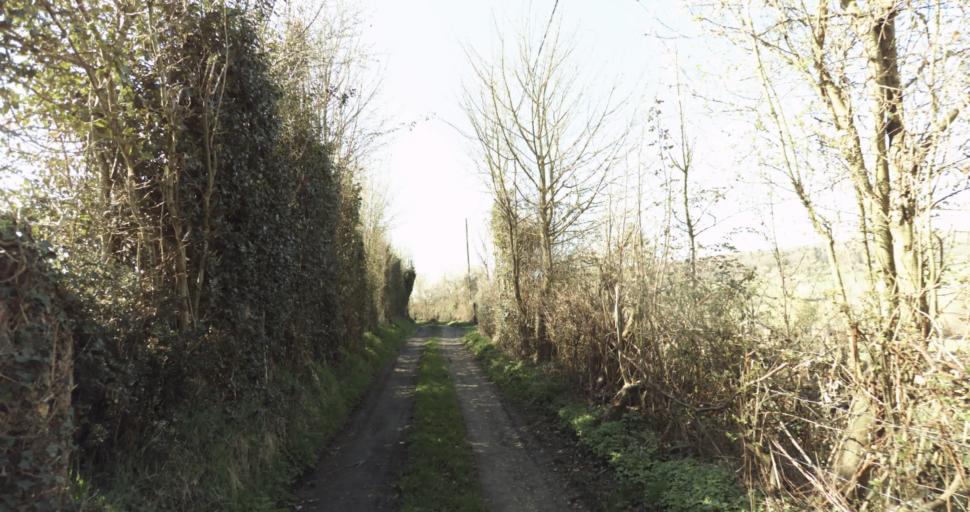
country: FR
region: Lower Normandy
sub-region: Departement du Calvados
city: Livarot
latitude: 48.9865
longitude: 0.0667
